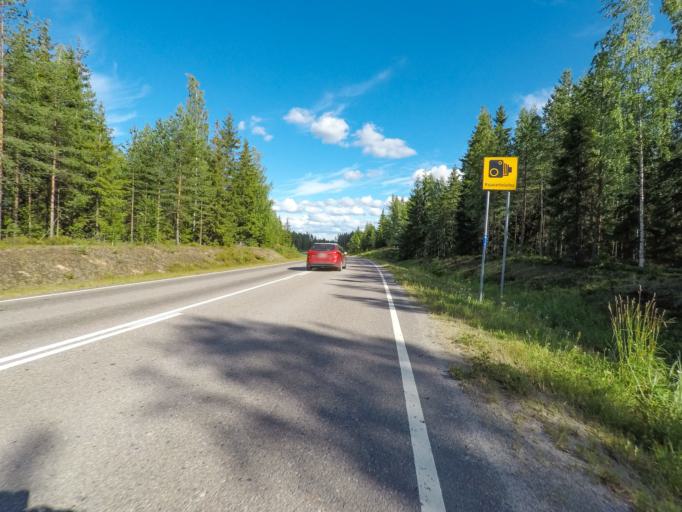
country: FI
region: South Karelia
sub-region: Lappeenranta
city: Joutseno
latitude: 61.1470
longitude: 28.6188
